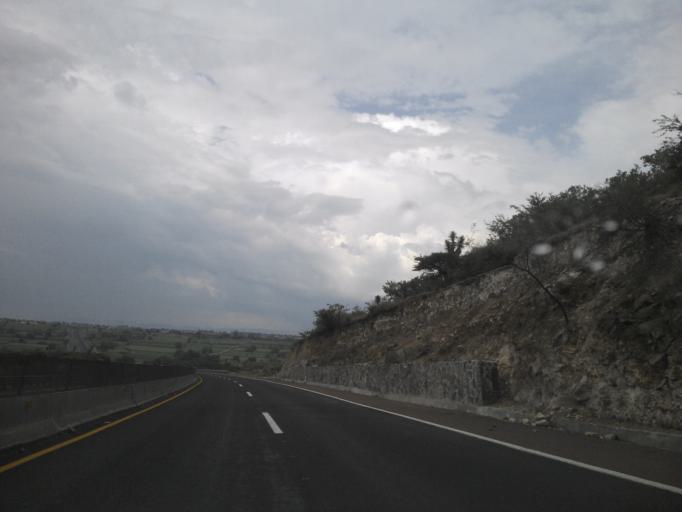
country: MX
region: Hidalgo
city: San Marcos
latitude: 20.0746
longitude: -99.3548
